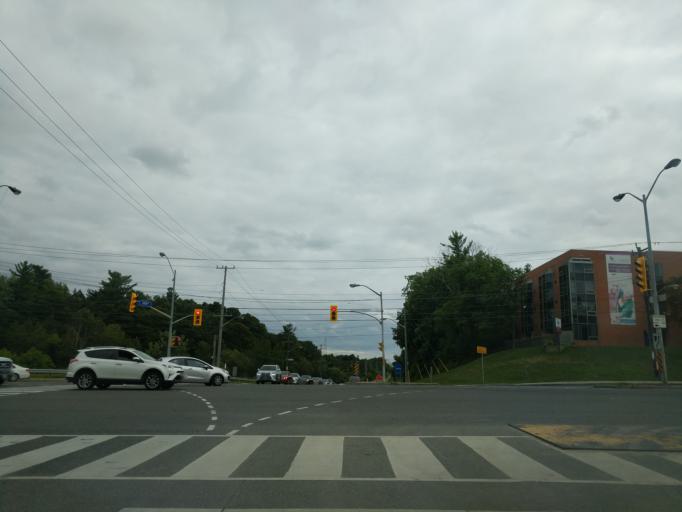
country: CA
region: Ontario
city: Willowdale
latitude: 43.8088
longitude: -79.3727
